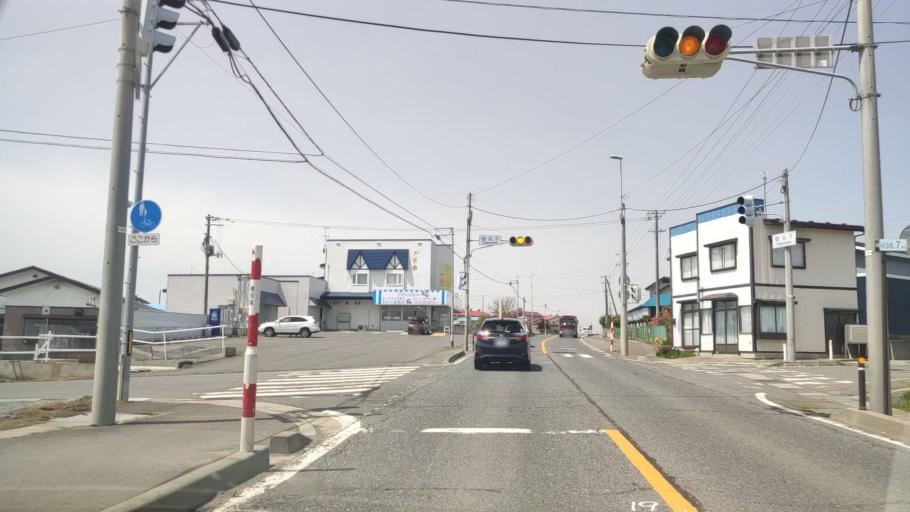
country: JP
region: Aomori
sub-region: Misawa Shi
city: Inuotose
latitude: 40.6074
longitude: 141.2872
